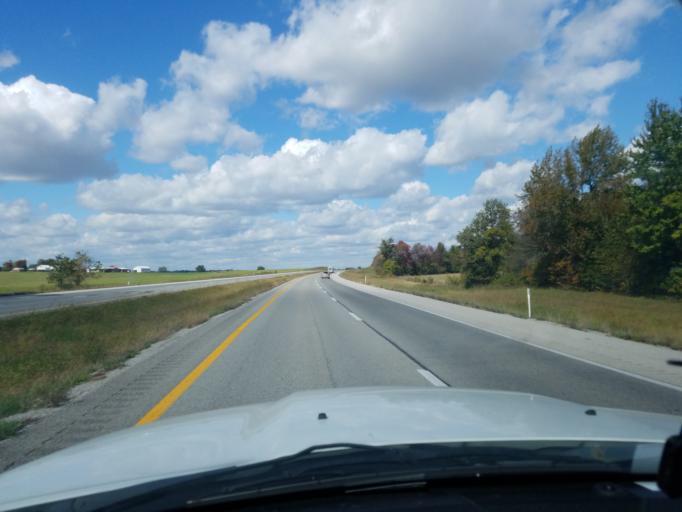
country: US
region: Kentucky
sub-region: Daviess County
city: Masonville
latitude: 37.6697
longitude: -87.0240
